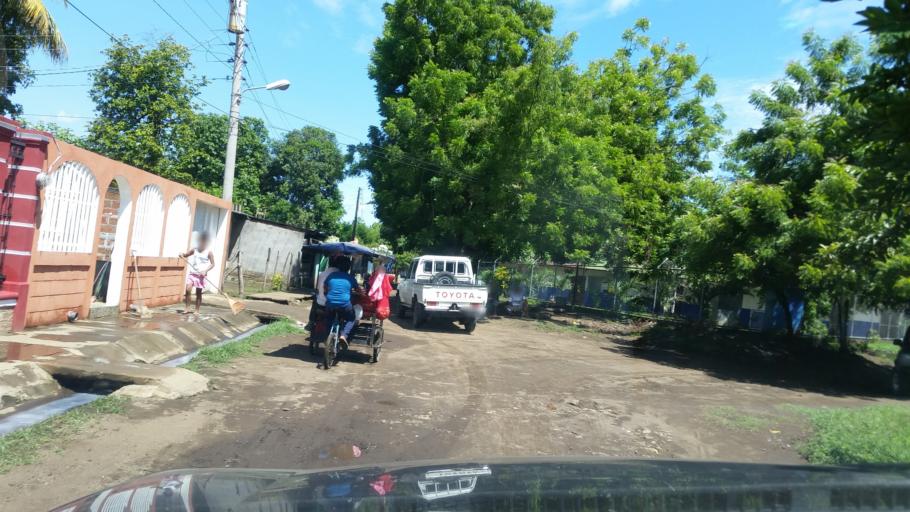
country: NI
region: Chinandega
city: Puerto Morazan
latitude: 12.7654
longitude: -87.1351
